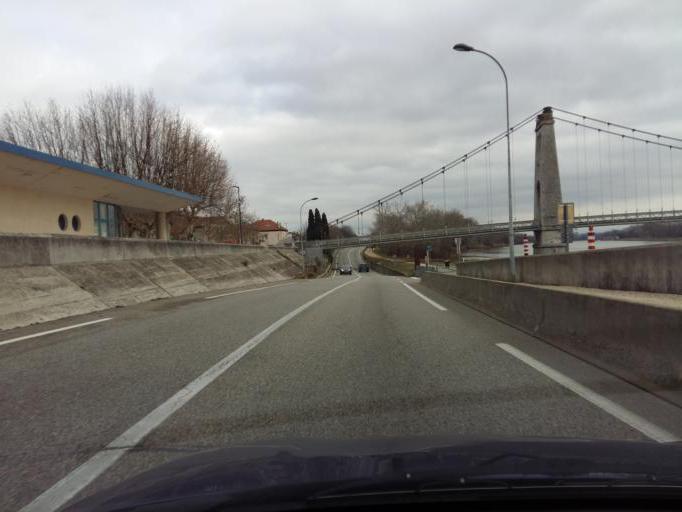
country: FR
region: Rhone-Alpes
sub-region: Departement de l'Ardeche
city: La Voulte-sur-Rhone
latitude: 44.8002
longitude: 4.7823
